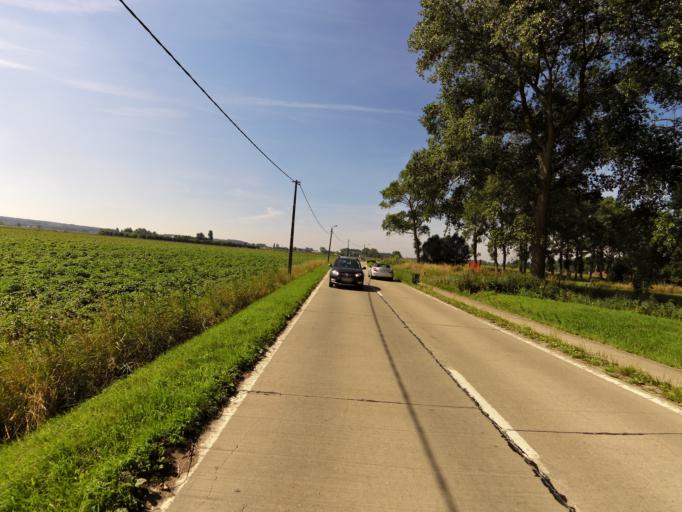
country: BE
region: Flanders
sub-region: Provincie West-Vlaanderen
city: Damme
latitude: 51.2576
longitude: 3.2602
